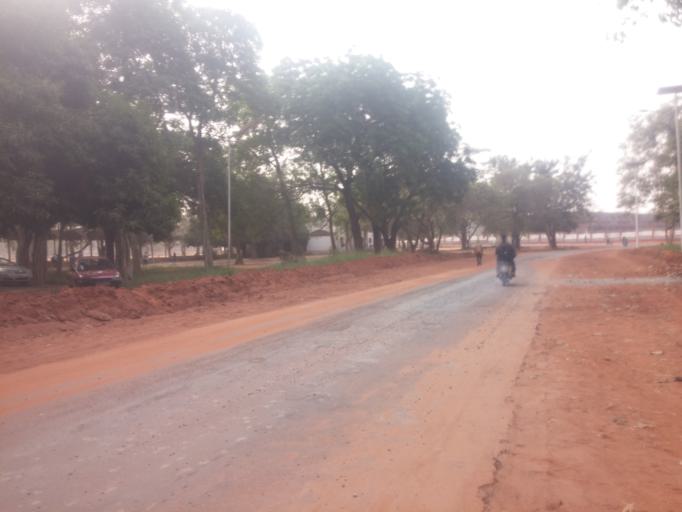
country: TG
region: Maritime
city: Lome
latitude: 6.1718
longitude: 1.2154
